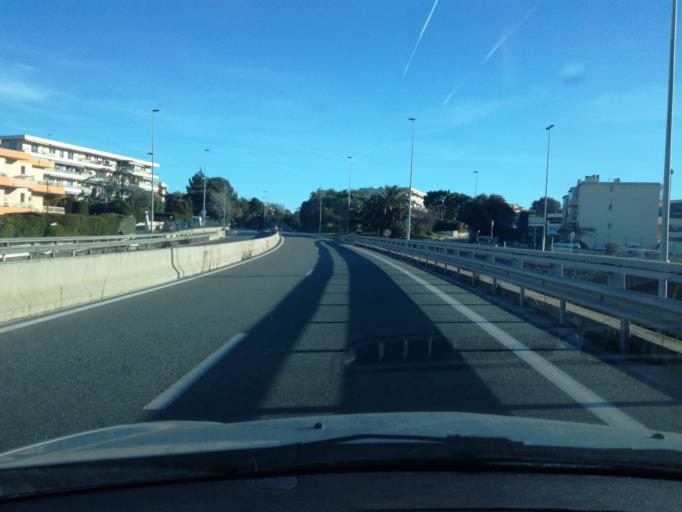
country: FR
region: Provence-Alpes-Cote d'Azur
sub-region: Departement des Alpes-Maritimes
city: Antibes
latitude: 43.5780
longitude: 7.1064
